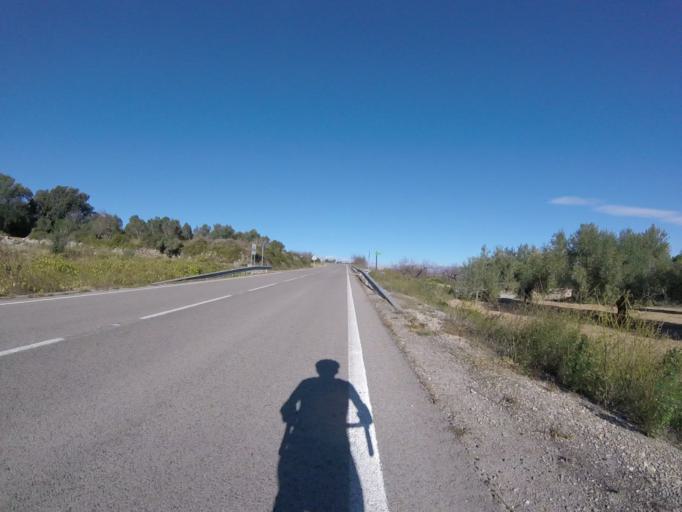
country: ES
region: Valencia
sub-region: Provincia de Castello
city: Cervera del Maestre
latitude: 40.4711
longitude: 0.2416
